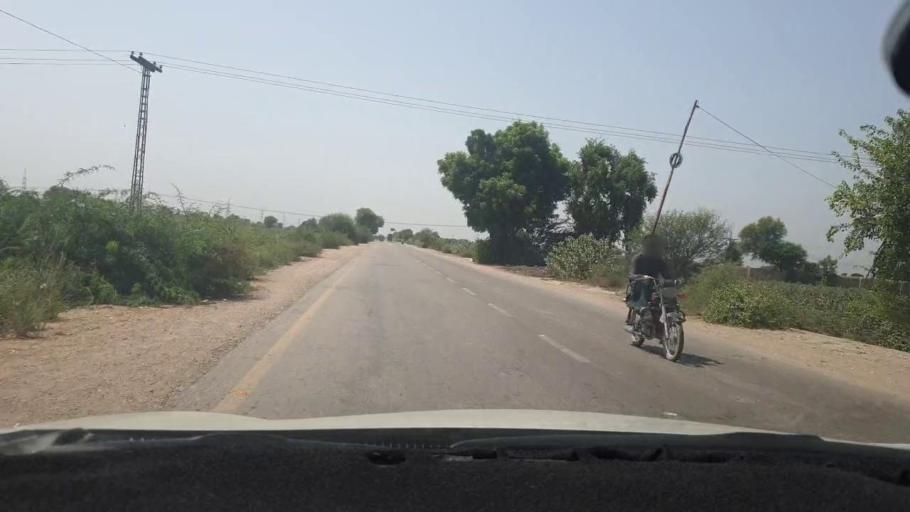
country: PK
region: Sindh
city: Bhit Shah
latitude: 25.8514
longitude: 68.4896
